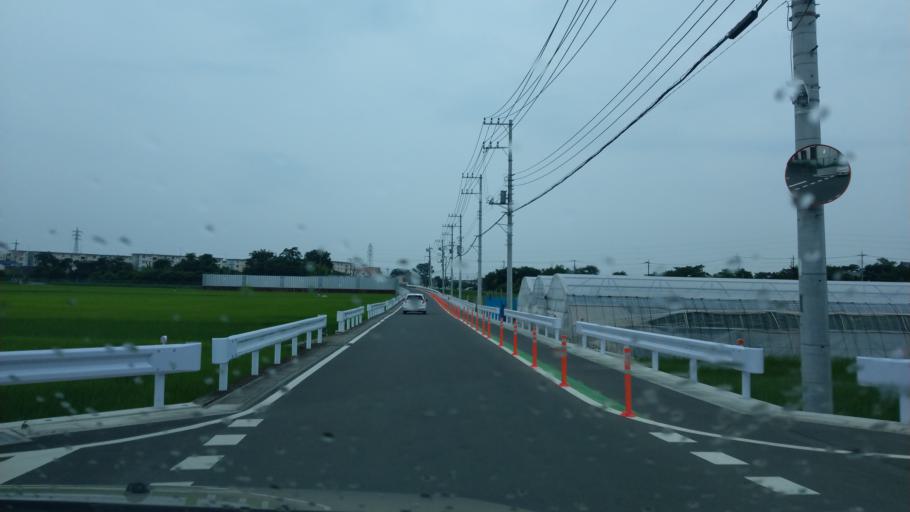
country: JP
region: Saitama
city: Yono
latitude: 35.8929
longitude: 139.5993
